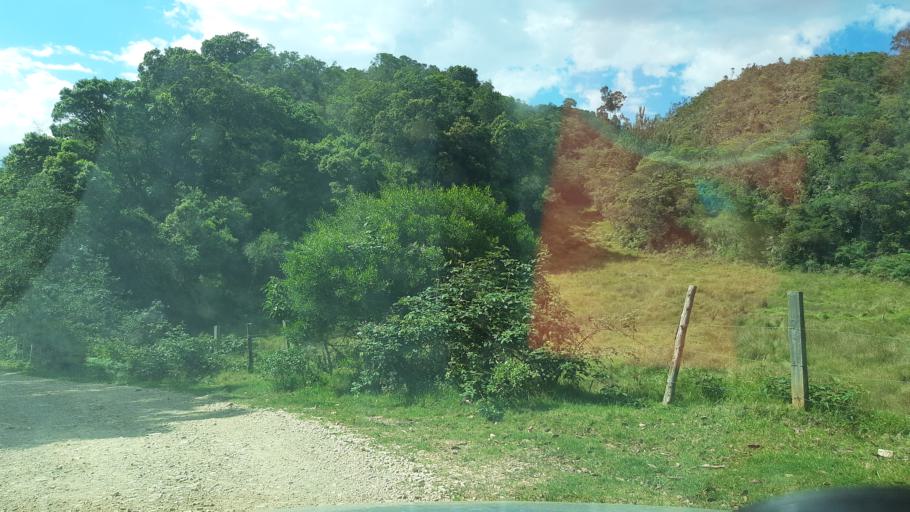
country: CO
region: Boyaca
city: La Capilla
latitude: 5.7179
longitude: -73.5358
